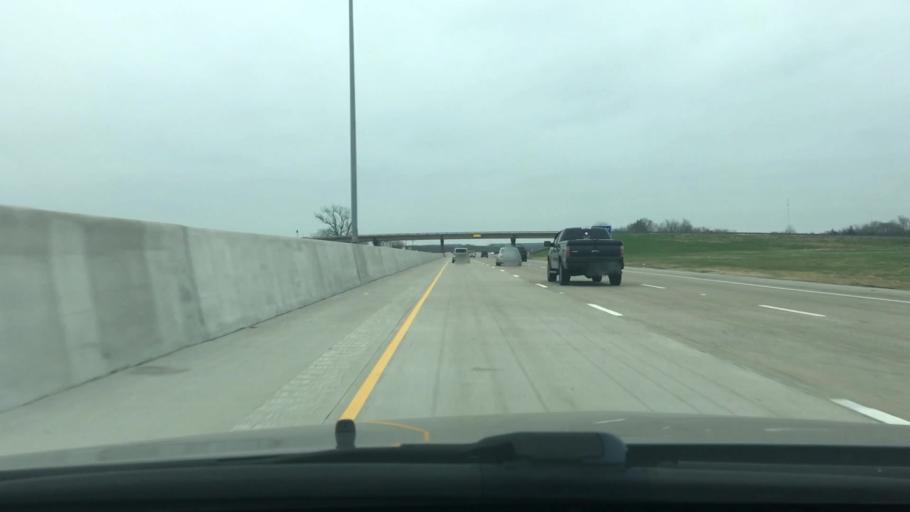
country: US
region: Texas
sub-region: Freestone County
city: Wortham
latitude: 31.9288
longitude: -96.4201
